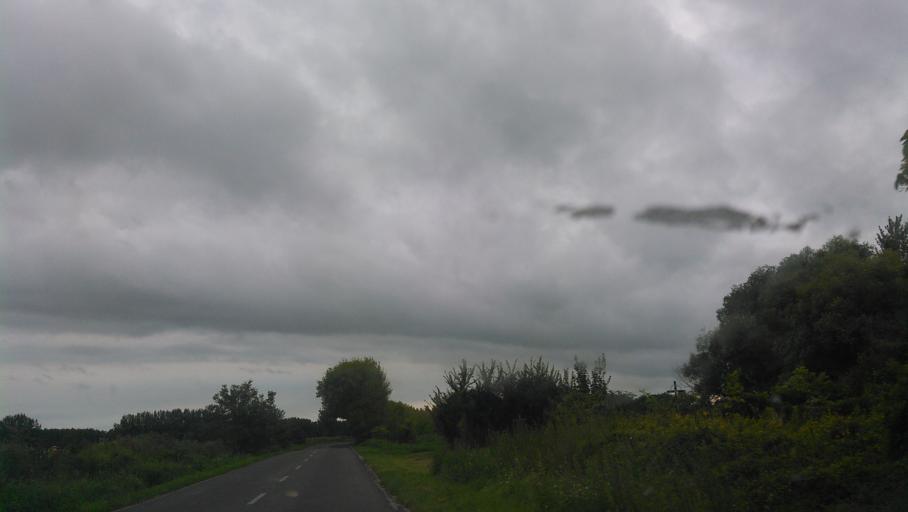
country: SK
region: Trnavsky
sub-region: Okres Dunajska Streda
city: Velky Meder
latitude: 47.9138
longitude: 17.7552
